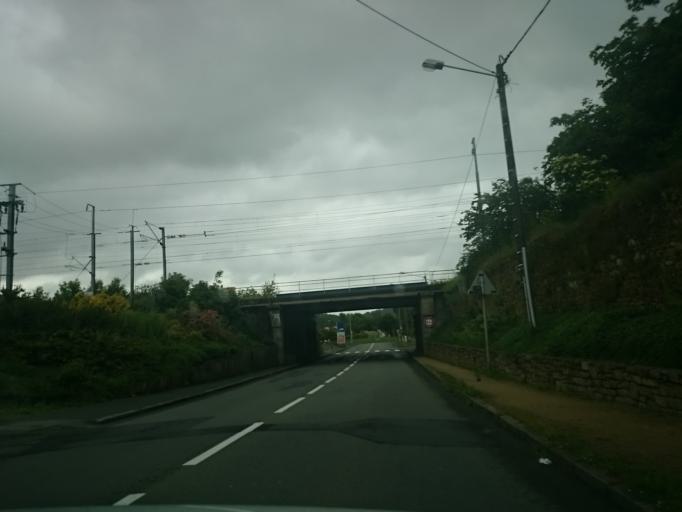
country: FR
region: Brittany
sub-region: Departement des Cotes-d'Armor
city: Guingamp
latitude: 48.5540
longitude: -3.1497
